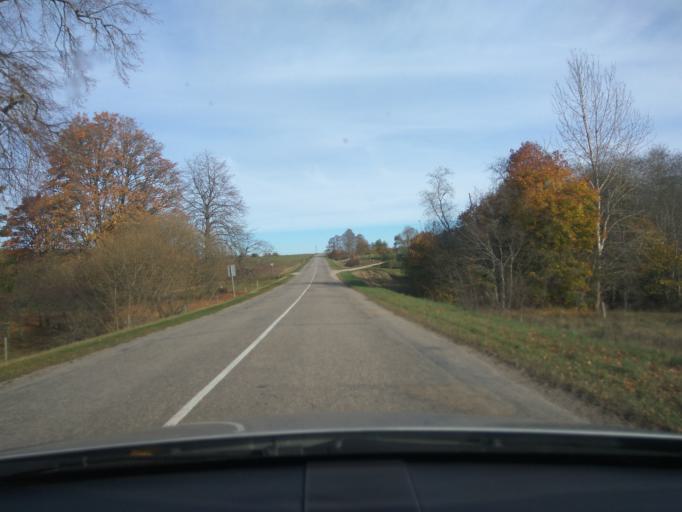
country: LV
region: Alsunga
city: Alsunga
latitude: 56.9845
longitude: 21.5743
